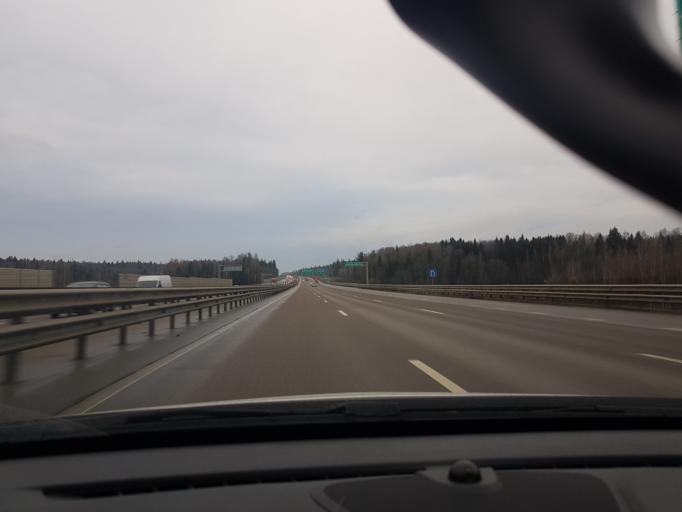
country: RU
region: Moskovskaya
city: Kostrovo
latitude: 55.8862
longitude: 36.6609
